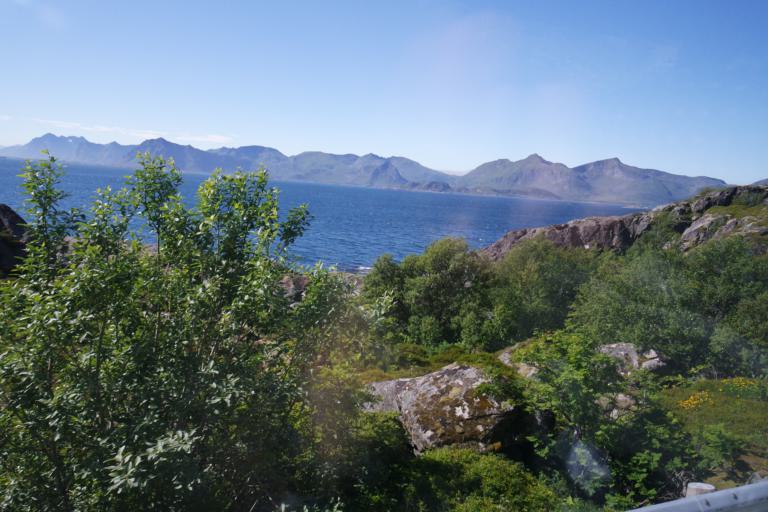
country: NO
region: Nordland
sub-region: Vagan
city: Kabelvag
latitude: 68.1924
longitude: 14.2168
